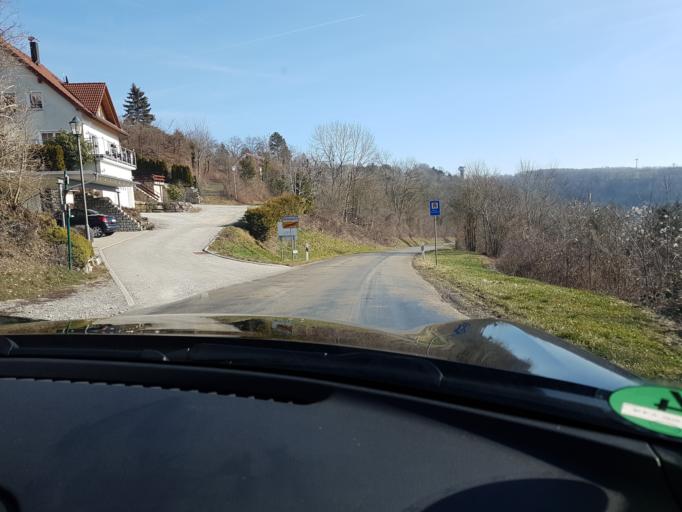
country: DE
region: Baden-Wuerttemberg
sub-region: Regierungsbezirk Stuttgart
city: Langenburg
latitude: 49.2522
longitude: 9.8509
